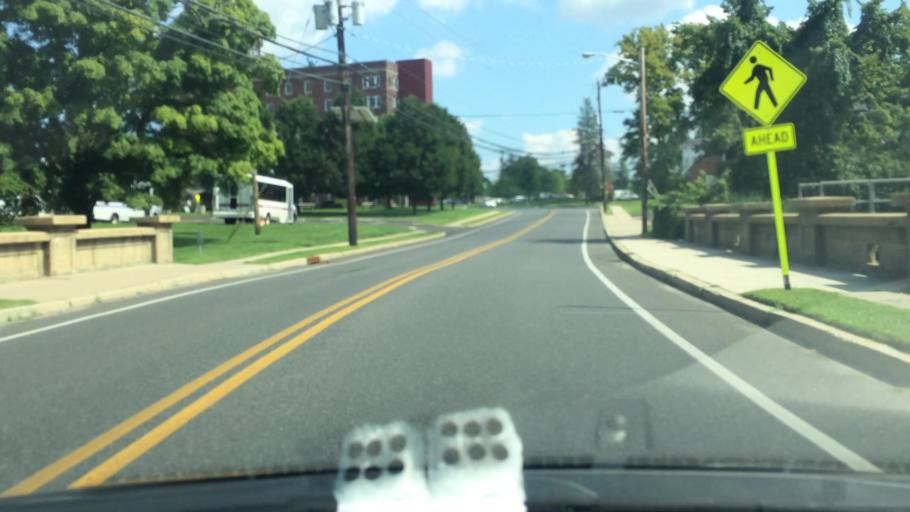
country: US
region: New Jersey
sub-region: Camden County
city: Blackwood
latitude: 39.7864
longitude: -75.0714
